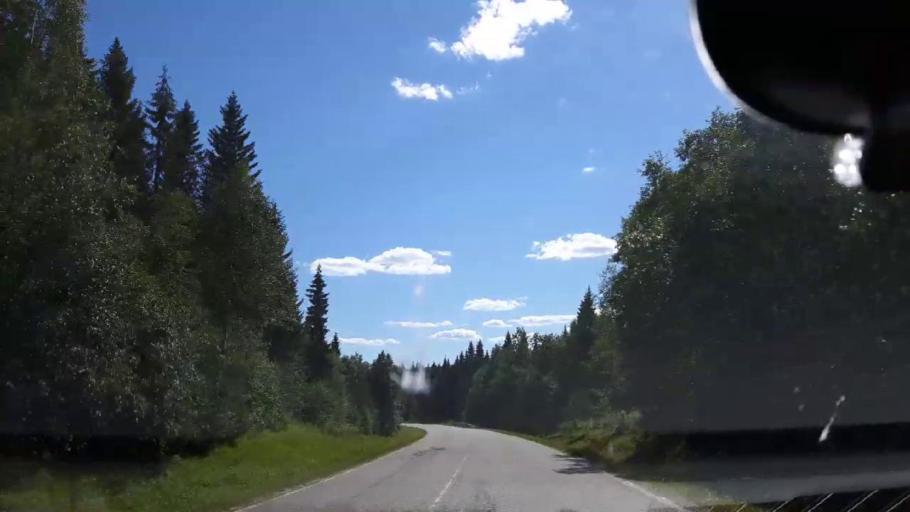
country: SE
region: Vaesternorrland
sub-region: Ange Kommun
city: Fransta
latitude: 62.8007
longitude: 16.2068
